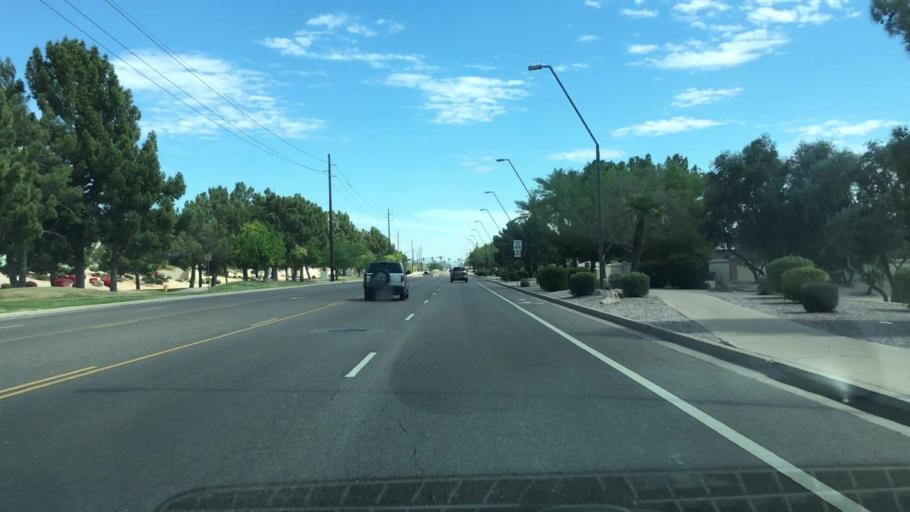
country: US
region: Arizona
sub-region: Maricopa County
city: Gilbert
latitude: 33.3642
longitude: -111.8156
